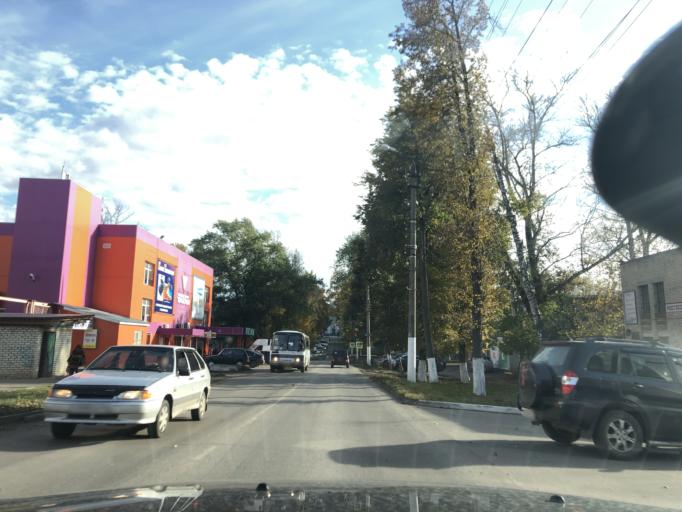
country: RU
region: Tula
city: Kireyevsk
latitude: 53.9301
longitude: 37.9277
